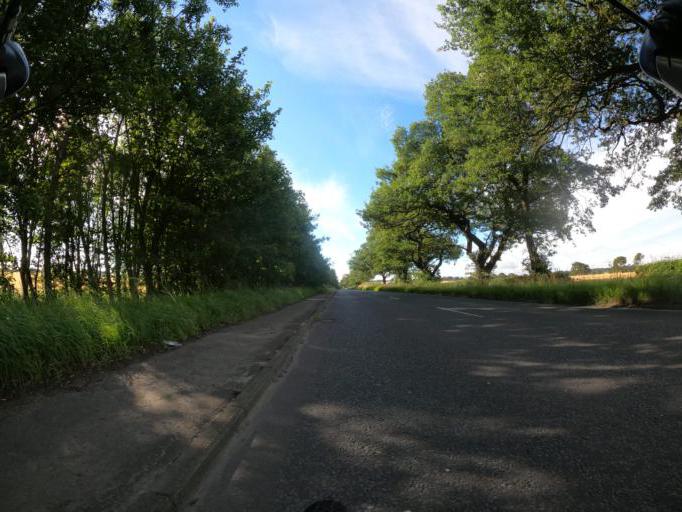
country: GB
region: Scotland
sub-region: Edinburgh
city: Newbridge
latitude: 55.9228
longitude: -3.4129
